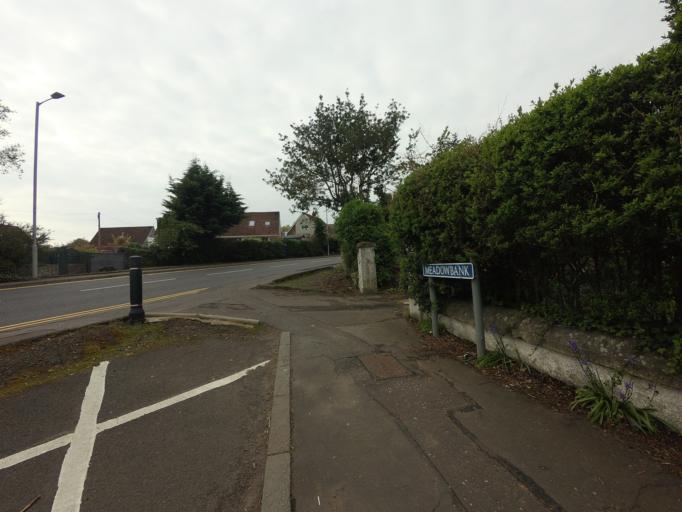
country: GB
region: Scotland
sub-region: Falkirk
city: Polmont
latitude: 55.9856
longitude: -3.7137
